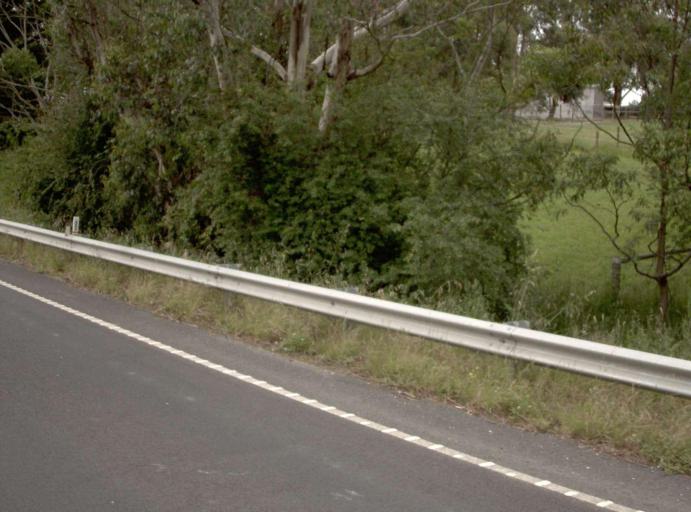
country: AU
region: Victoria
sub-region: Bass Coast
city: North Wonthaggi
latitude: -38.5802
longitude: 145.9889
